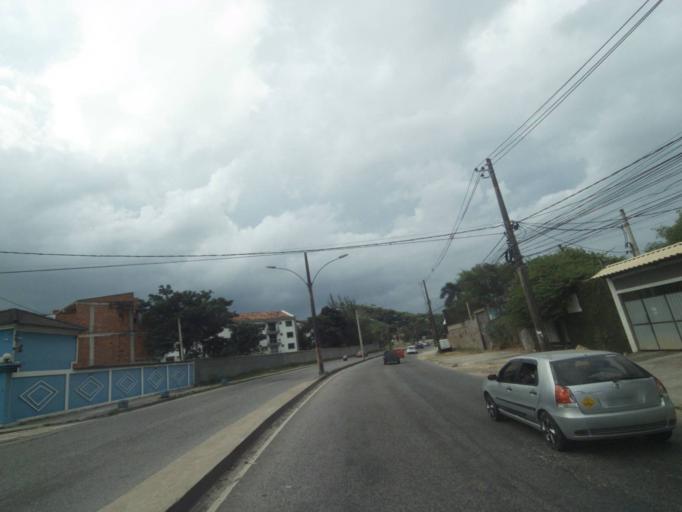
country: BR
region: Rio de Janeiro
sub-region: Nilopolis
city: Nilopolis
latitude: -22.8952
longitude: -43.3980
